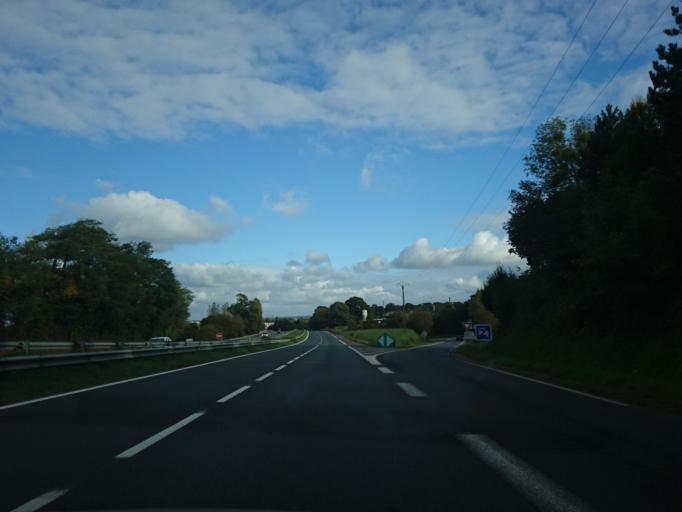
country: FR
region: Brittany
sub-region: Departement des Cotes-d'Armor
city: Graces
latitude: 48.5653
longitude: -3.2131
